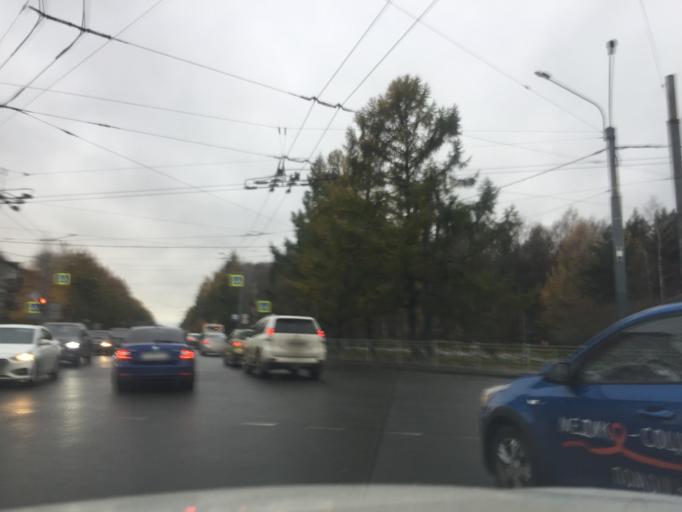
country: RU
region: St.-Petersburg
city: Sosnovka
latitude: 60.0188
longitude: 30.3673
